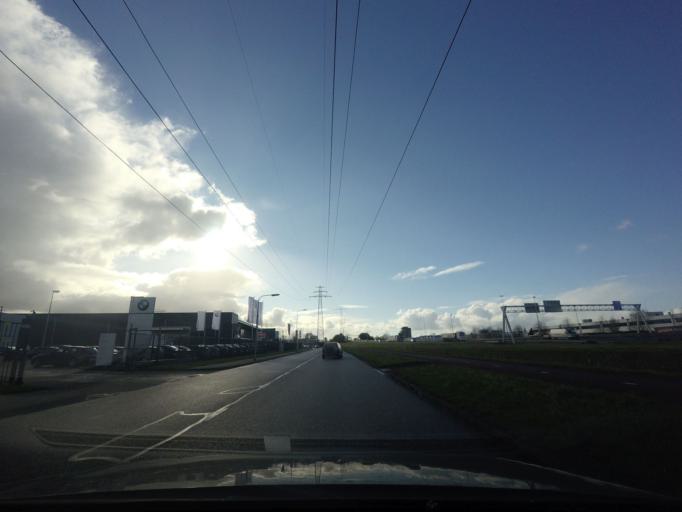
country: NL
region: Groningen
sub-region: Gemeente Groningen
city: Oosterpark
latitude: 53.2162
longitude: 6.6086
